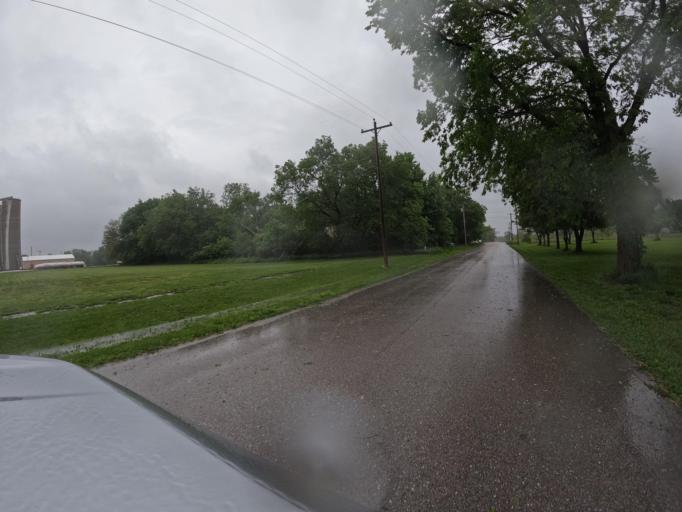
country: US
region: Nebraska
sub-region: Gage County
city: Wymore
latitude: 40.1402
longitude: -96.6683
